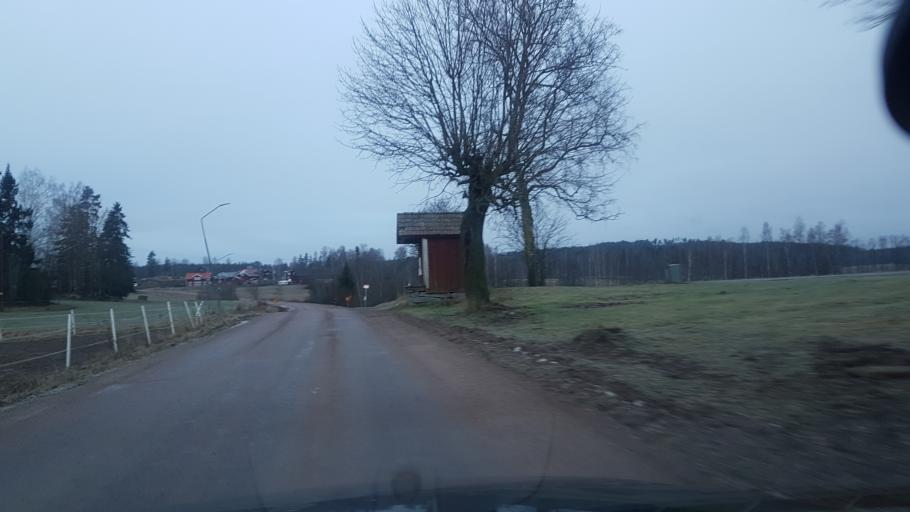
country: SE
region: Dalarna
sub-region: Borlange Kommun
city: Ornas
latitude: 60.4450
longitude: 15.6403
